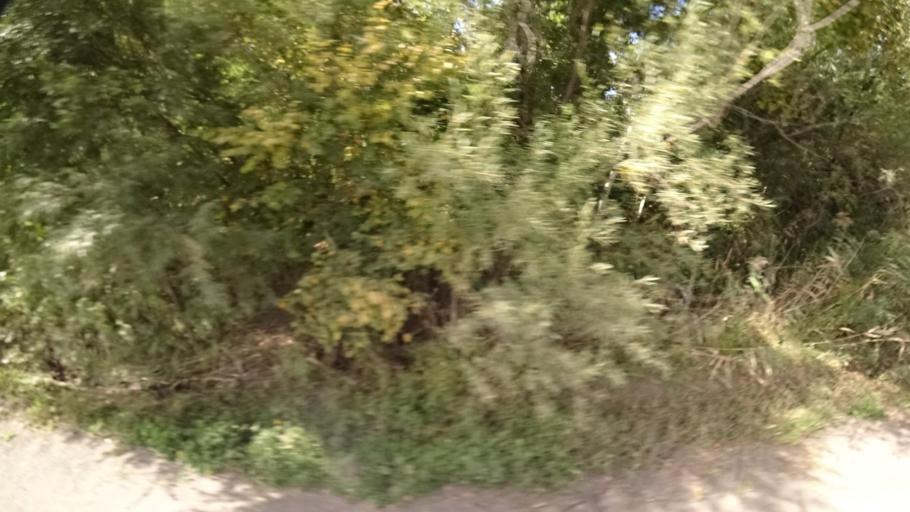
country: RU
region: Primorskiy
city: Yakovlevka
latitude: 44.3900
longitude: 133.5471
